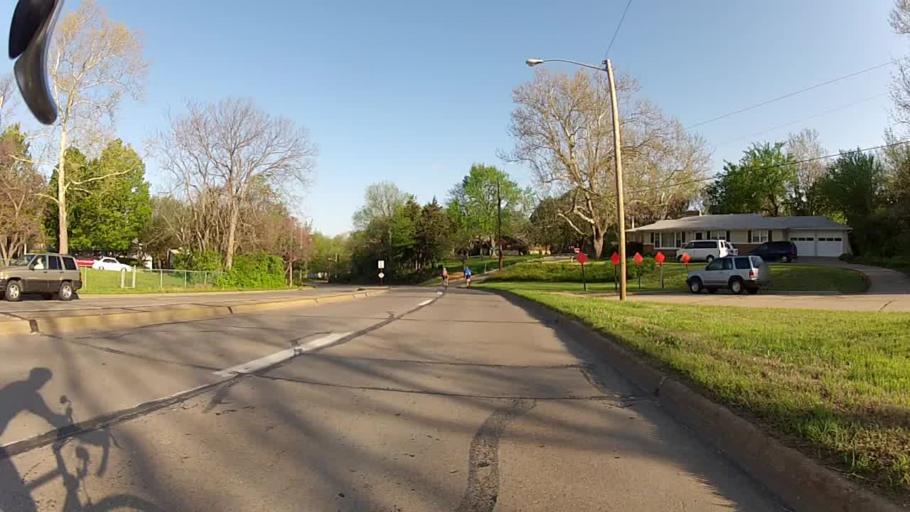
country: US
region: Kansas
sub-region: Riley County
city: Manhattan
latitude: 39.1897
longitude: -96.5999
